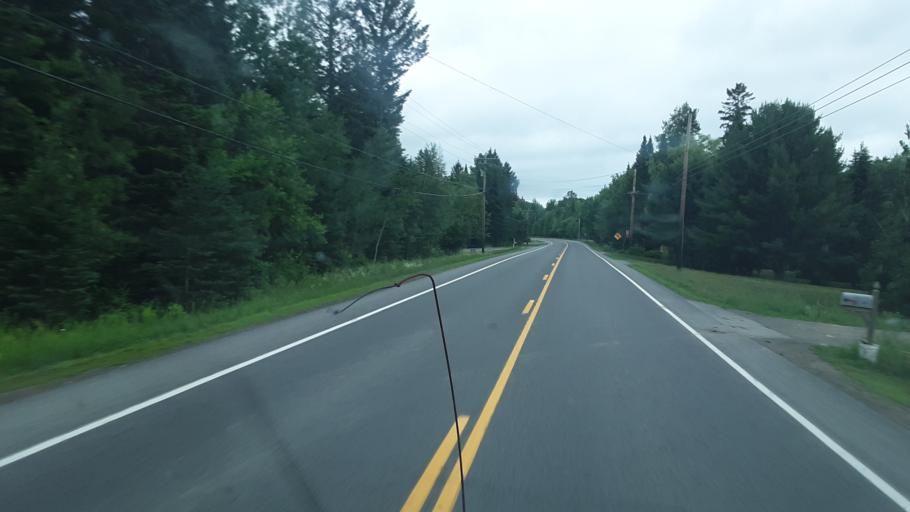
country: US
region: Maine
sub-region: Penobscot County
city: Patten
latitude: 45.9326
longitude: -68.4483
